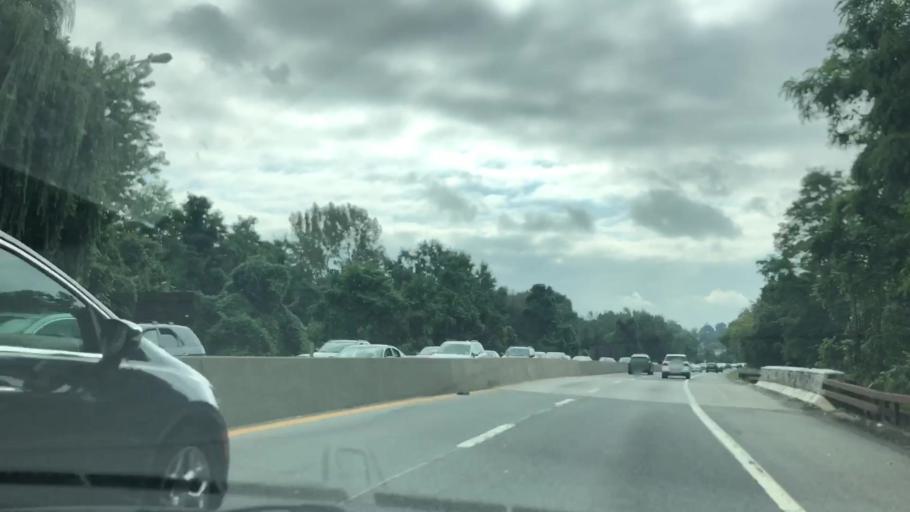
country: US
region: New York
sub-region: Westchester County
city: Hastings-on-Hudson
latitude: 40.9653
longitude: -73.8711
